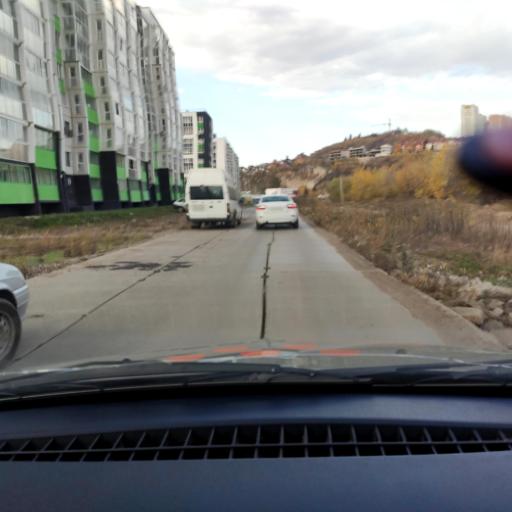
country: RU
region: Bashkortostan
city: Ufa
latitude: 54.6916
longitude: 55.9732
